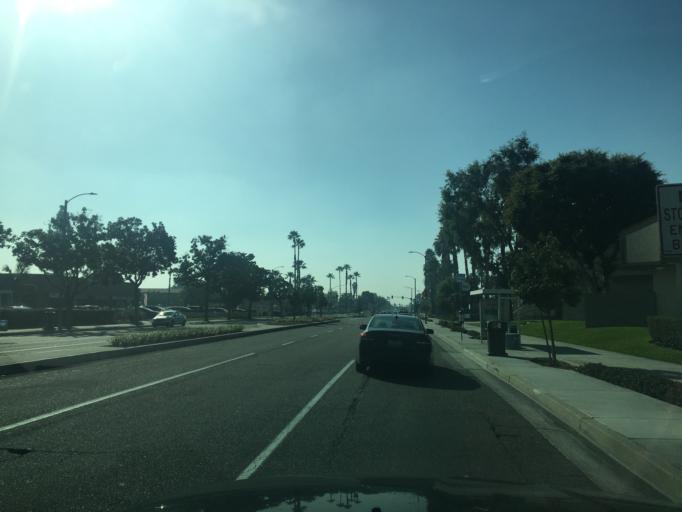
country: US
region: California
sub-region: Orange County
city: Tustin
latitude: 33.7437
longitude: -117.8166
